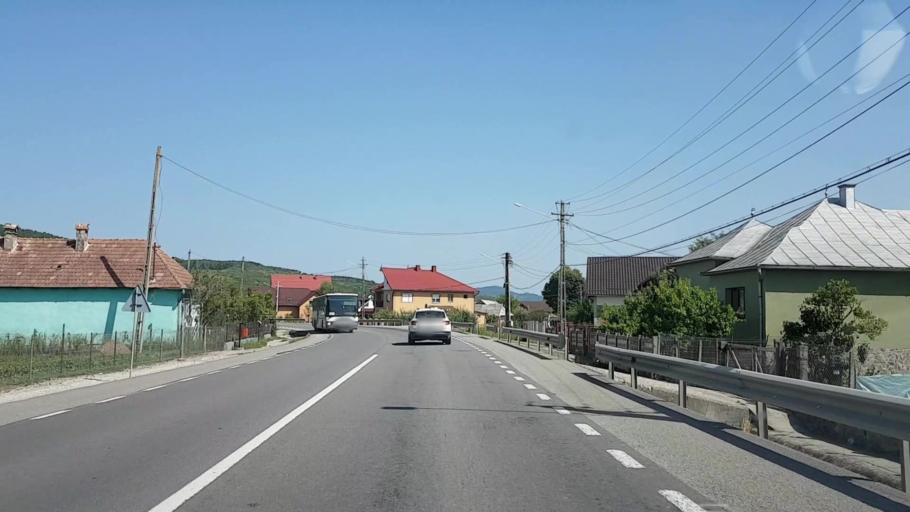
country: RO
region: Bistrita-Nasaud
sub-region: Comuna Sintereag
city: Sintereag
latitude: 47.1788
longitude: 24.2948
